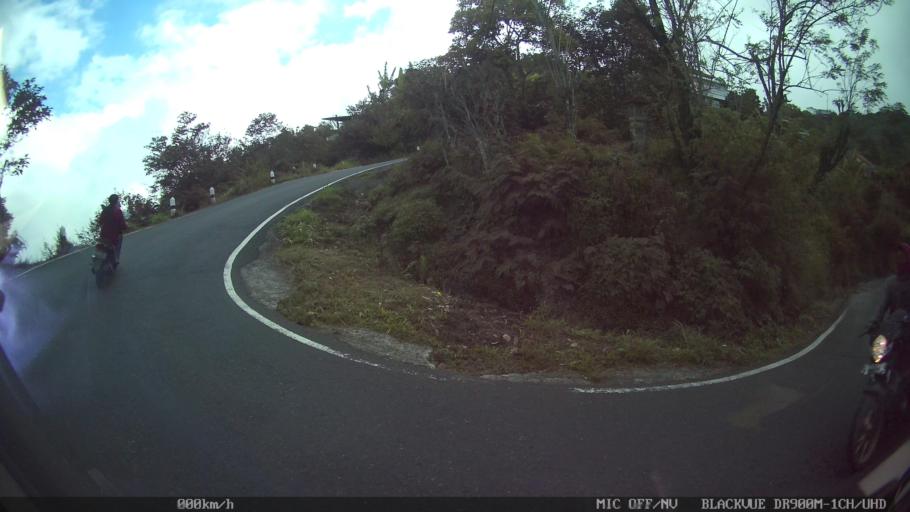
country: ID
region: Bali
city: Banjar Kedisan
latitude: -8.2596
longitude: 115.3418
